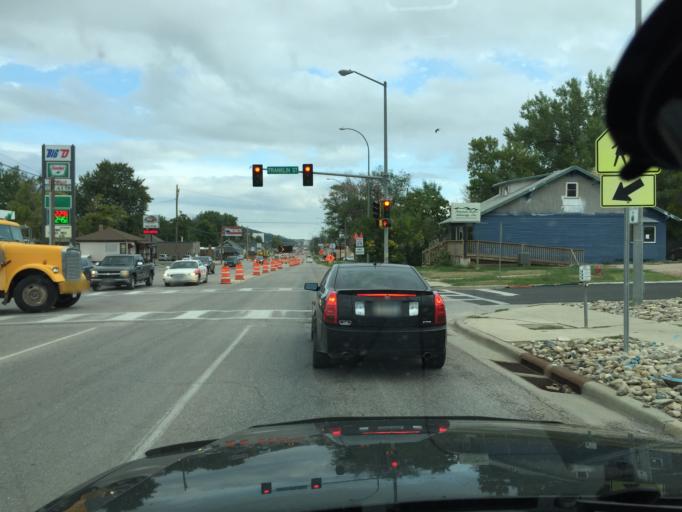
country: US
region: South Dakota
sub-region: Pennington County
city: Rapid City
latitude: 44.0704
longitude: -103.2323
